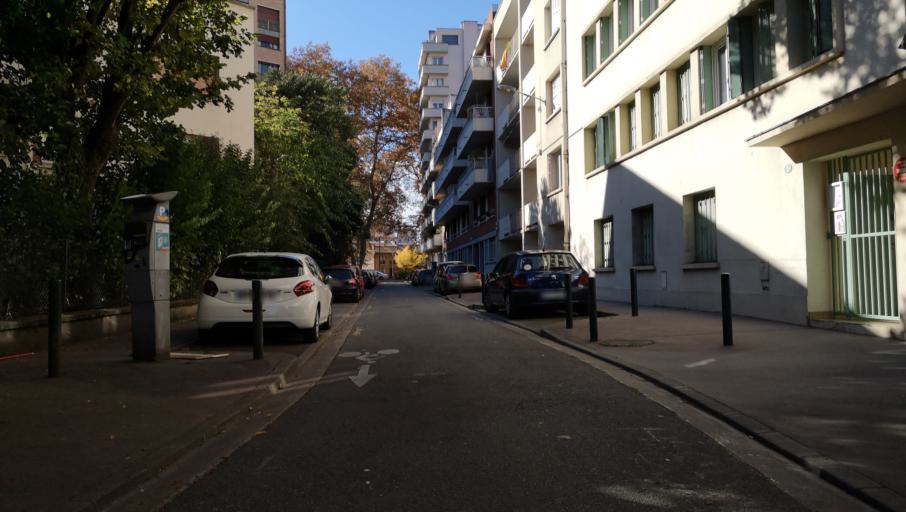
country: FR
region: Midi-Pyrenees
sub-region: Departement de la Haute-Garonne
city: Toulouse
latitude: 43.6068
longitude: 1.4328
